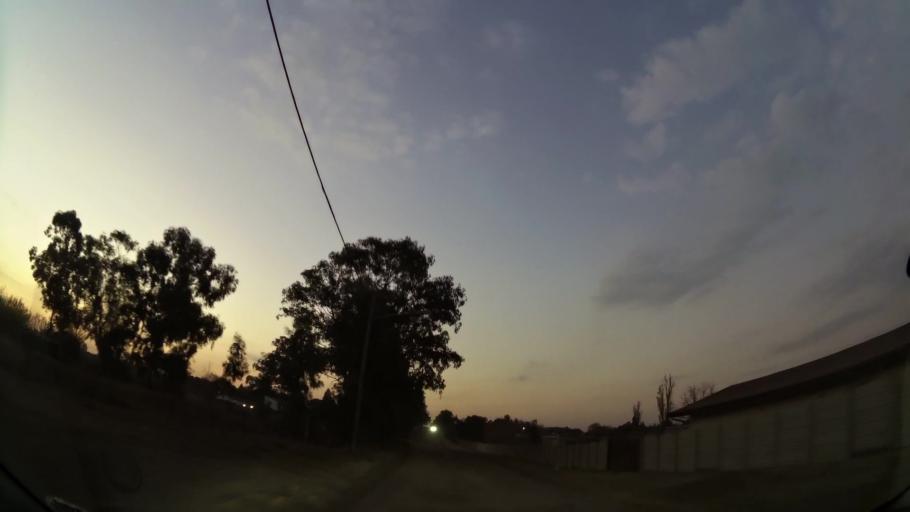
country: ZA
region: Gauteng
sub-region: Ekurhuleni Metropolitan Municipality
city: Benoni
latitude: -26.1240
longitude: 28.3058
